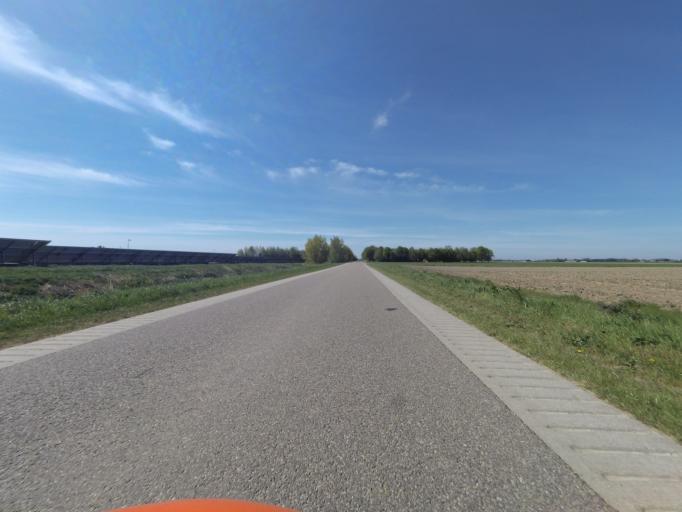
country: NL
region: Flevoland
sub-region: Gemeente Dronten
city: Biddinghuizen
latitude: 52.4281
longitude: 5.6890
